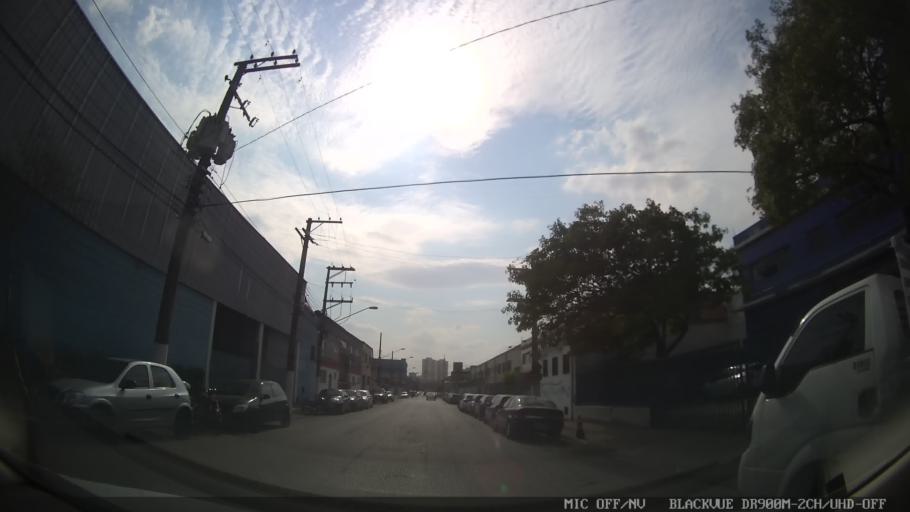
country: BR
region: Sao Paulo
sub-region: Sao Caetano Do Sul
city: Sao Caetano do Sul
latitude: -23.6005
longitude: -46.5933
